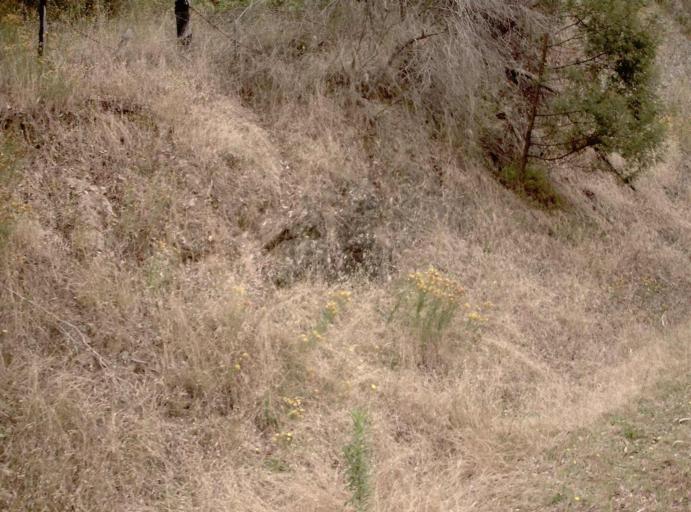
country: AU
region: Victoria
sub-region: Wellington
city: Heyfield
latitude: -37.6947
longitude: 146.6496
